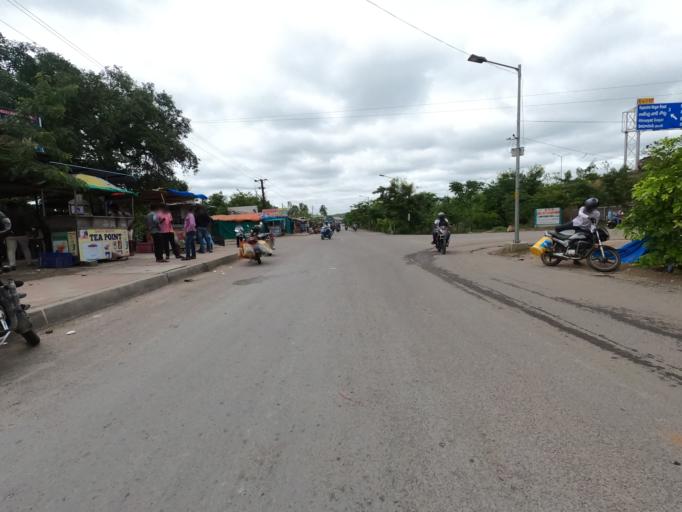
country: IN
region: Telangana
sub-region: Hyderabad
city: Hyderabad
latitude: 17.3385
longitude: 78.3673
